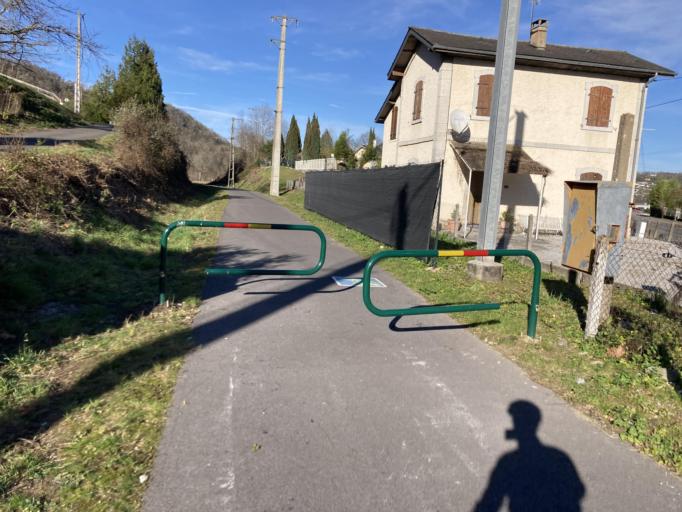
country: FR
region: Aquitaine
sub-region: Departement des Pyrenees-Atlantiques
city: Arudy
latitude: 43.1072
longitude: -0.4356
